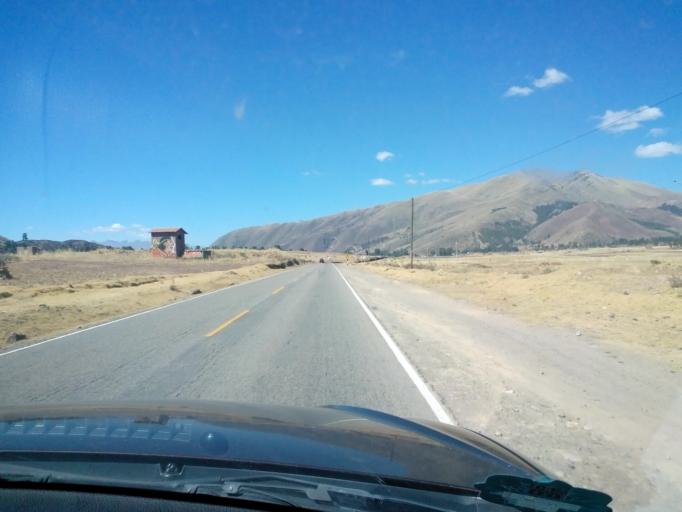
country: PE
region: Cusco
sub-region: Provincia de Canchis
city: Queromarca
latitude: -14.1636
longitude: -71.3848
